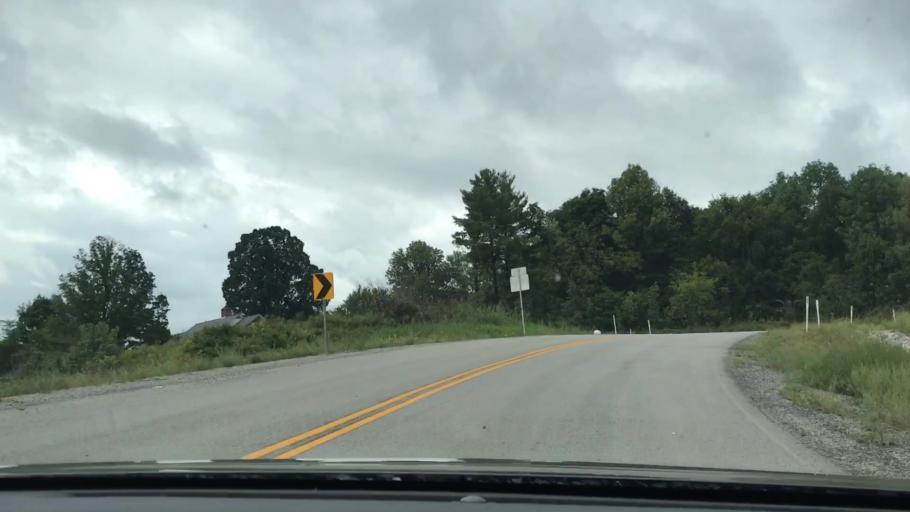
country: US
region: Kentucky
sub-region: Barren County
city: Glasgow
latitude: 36.9579
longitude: -85.8635
